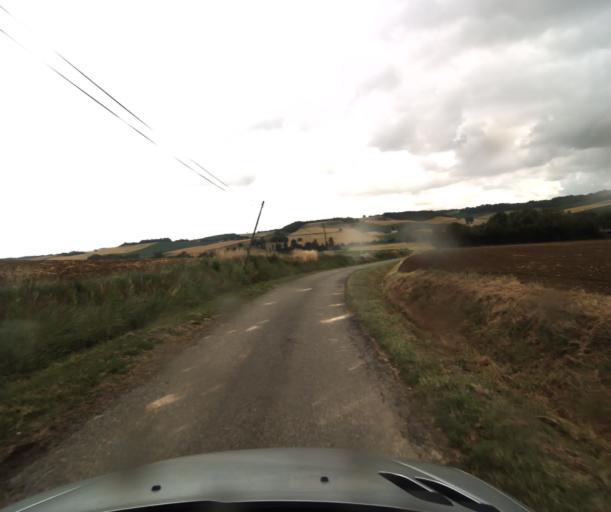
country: FR
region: Midi-Pyrenees
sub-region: Departement du Tarn-et-Garonne
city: Lavit
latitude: 43.9522
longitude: 0.9308
